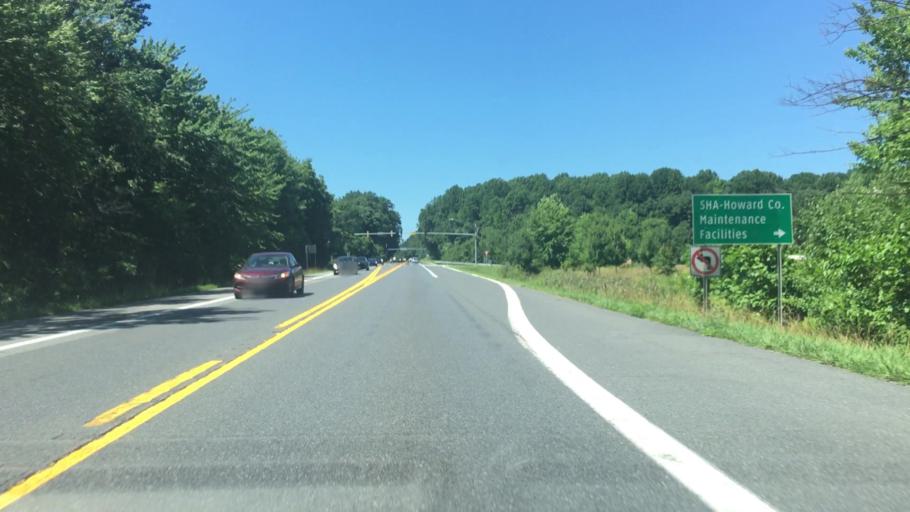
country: US
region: Maryland
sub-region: Howard County
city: Highland
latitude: 39.2481
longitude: -76.9784
